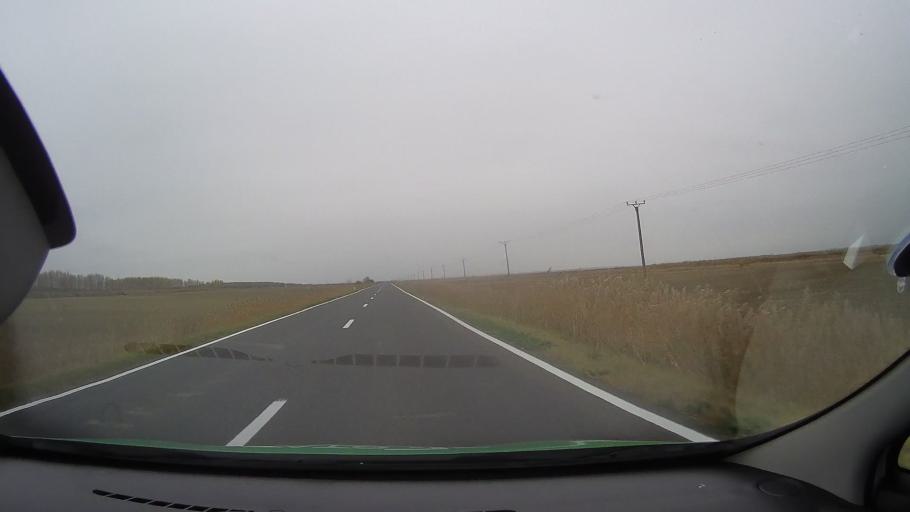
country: RO
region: Ialomita
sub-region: Comuna Giurgeni
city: Giurgeni
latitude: 44.7190
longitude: 27.8519
